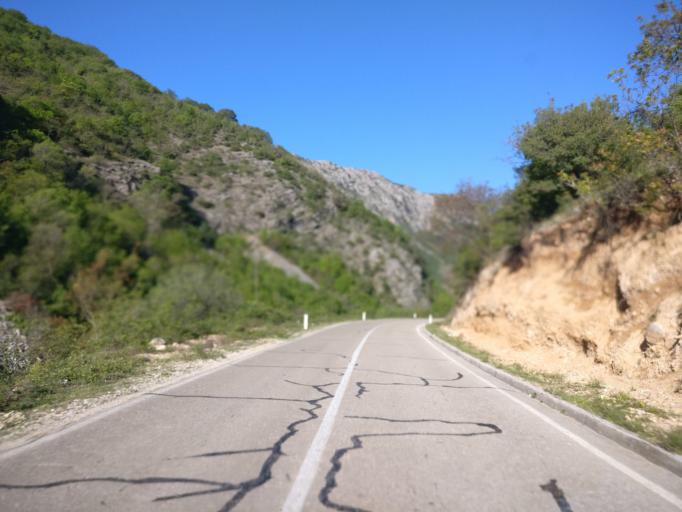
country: BA
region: Federation of Bosnia and Herzegovina
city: Stolac
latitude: 43.0720
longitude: 18.0469
